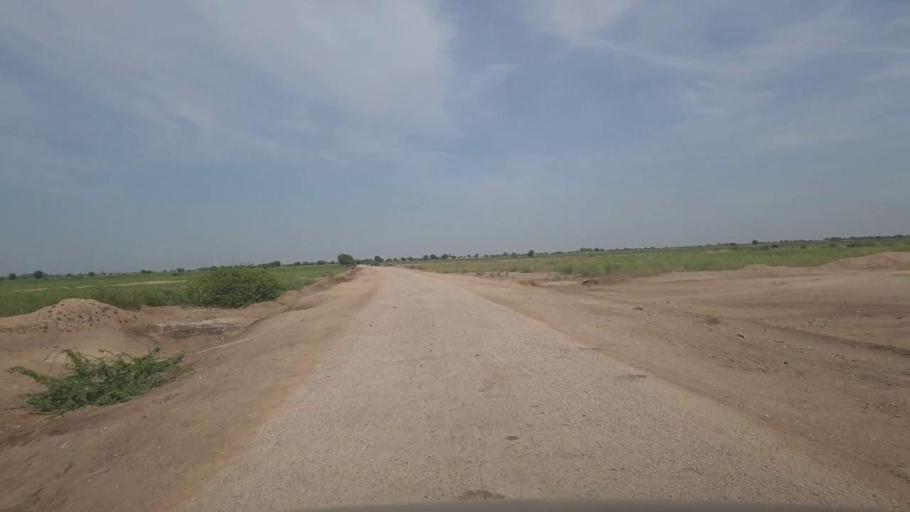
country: PK
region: Sindh
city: Kunri
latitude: 25.2335
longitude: 69.6252
